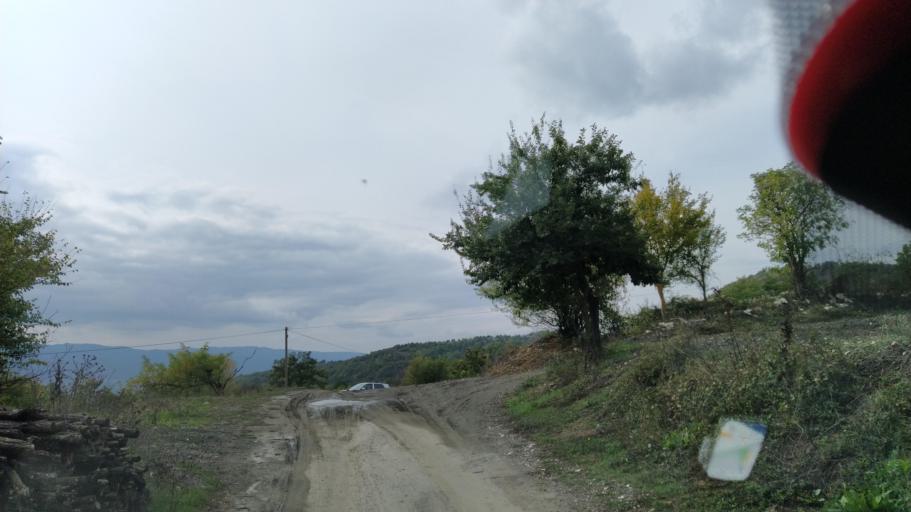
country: MK
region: Strumica
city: Veljusa
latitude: 41.5117
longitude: 22.4935
